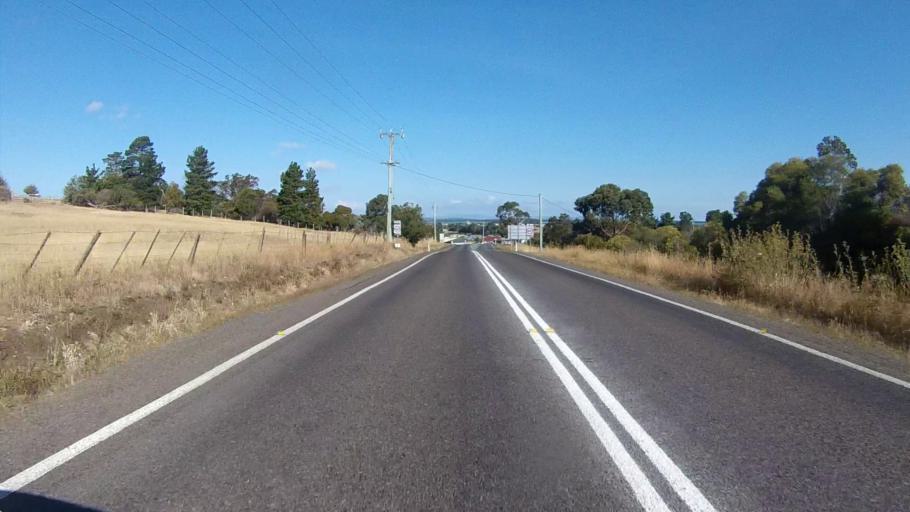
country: AU
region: Tasmania
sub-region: Sorell
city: Sorell
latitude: -42.7742
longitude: 147.5502
